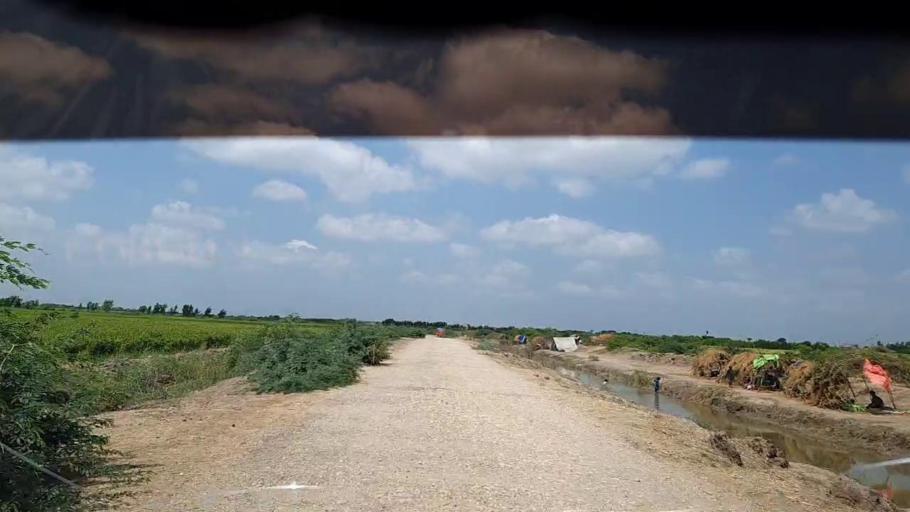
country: PK
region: Sindh
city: Kadhan
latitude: 24.5878
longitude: 68.9690
